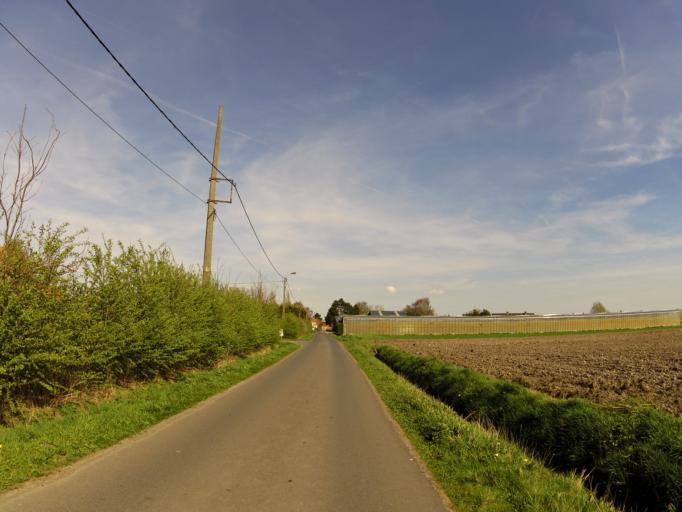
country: BE
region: Flanders
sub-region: Provincie West-Vlaanderen
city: Oudenburg
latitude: 51.1635
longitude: 3.0380
